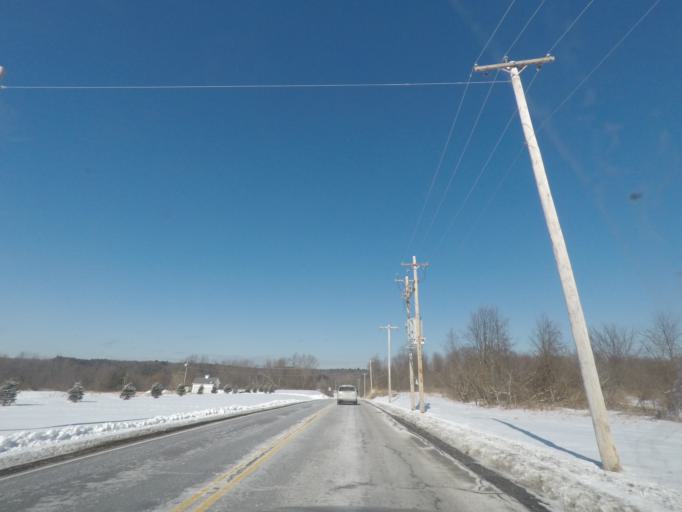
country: US
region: New York
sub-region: Saratoga County
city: Ballston Spa
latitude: 42.9926
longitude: -73.7990
